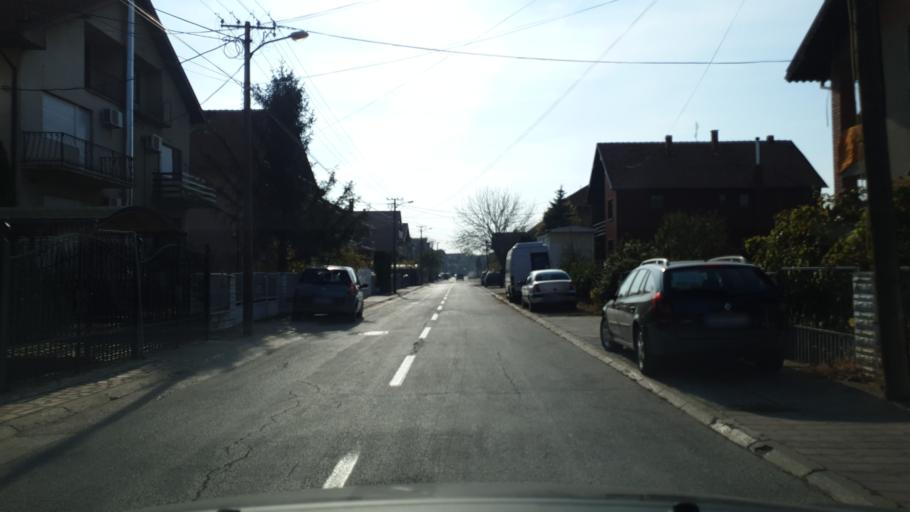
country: RS
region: Central Serbia
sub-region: Pomoravski Okrug
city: Paracin
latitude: 43.8595
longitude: 21.4249
